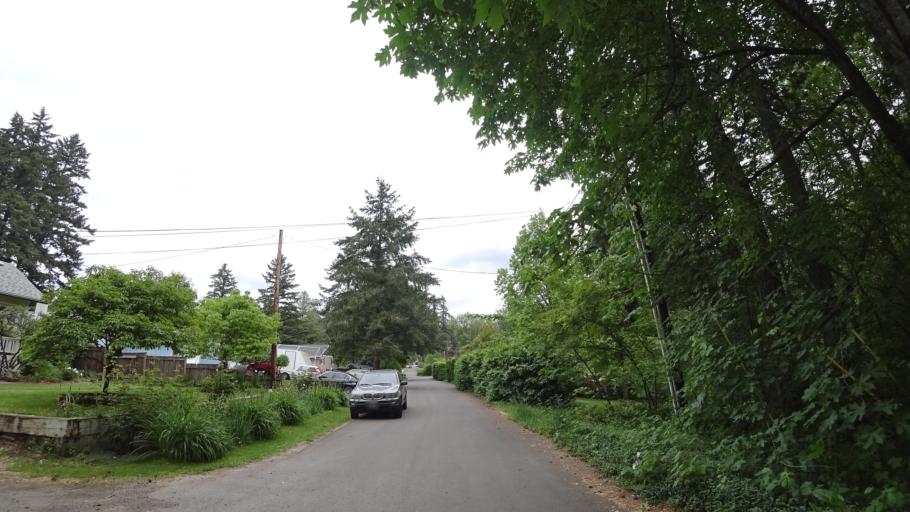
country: US
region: Oregon
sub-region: Washington County
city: Metzger
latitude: 45.4505
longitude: -122.7629
